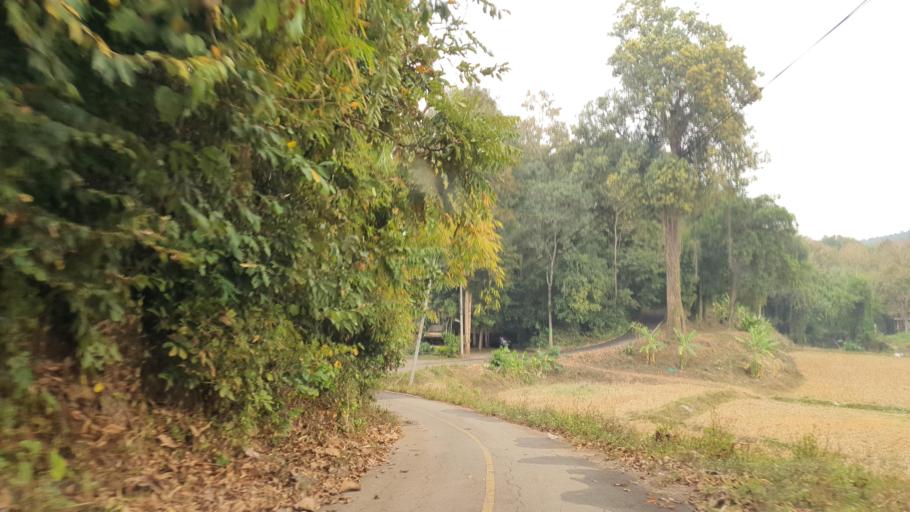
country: TH
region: Chiang Mai
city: Mae Wang
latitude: 18.6603
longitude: 98.6403
